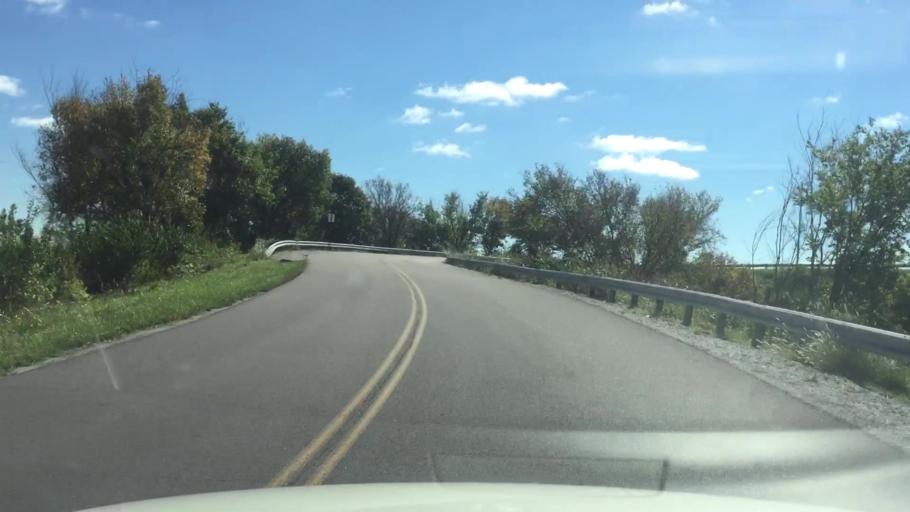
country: US
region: Missouri
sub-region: Boone County
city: Ashland
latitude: 38.7751
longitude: -92.2509
